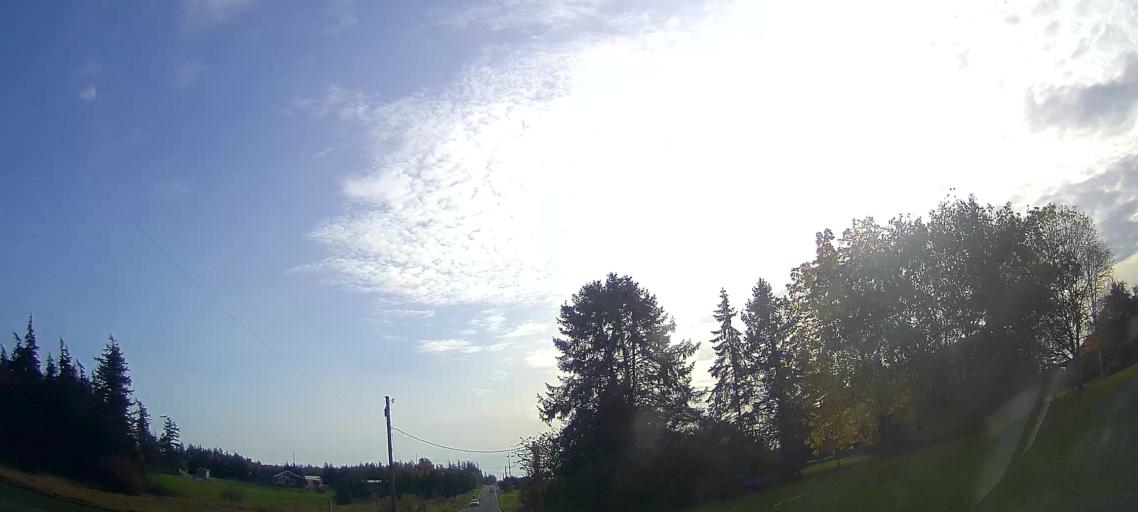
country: US
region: Washington
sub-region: Snohomish County
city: Stanwood
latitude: 48.2444
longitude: -122.4171
